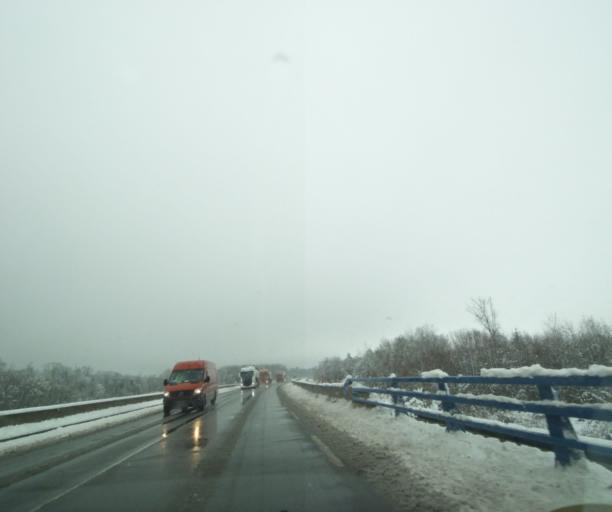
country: FR
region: Champagne-Ardenne
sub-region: Departement de la Haute-Marne
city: Villiers-en-Lieu
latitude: 48.5763
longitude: 4.8716
